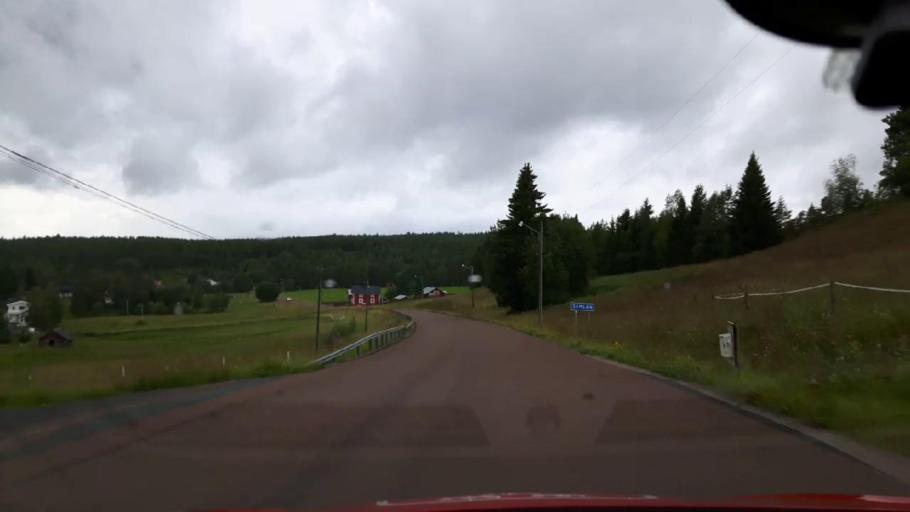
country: SE
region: Jaemtland
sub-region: Are Kommun
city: Jarpen
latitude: 63.3320
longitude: 13.7004
